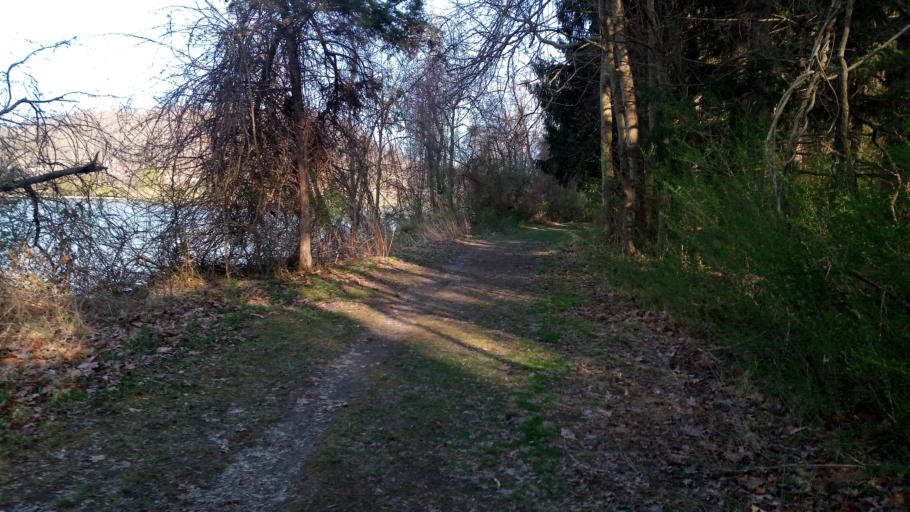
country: US
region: Pennsylvania
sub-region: York County
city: Jacobus
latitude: 39.8956
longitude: -76.7072
